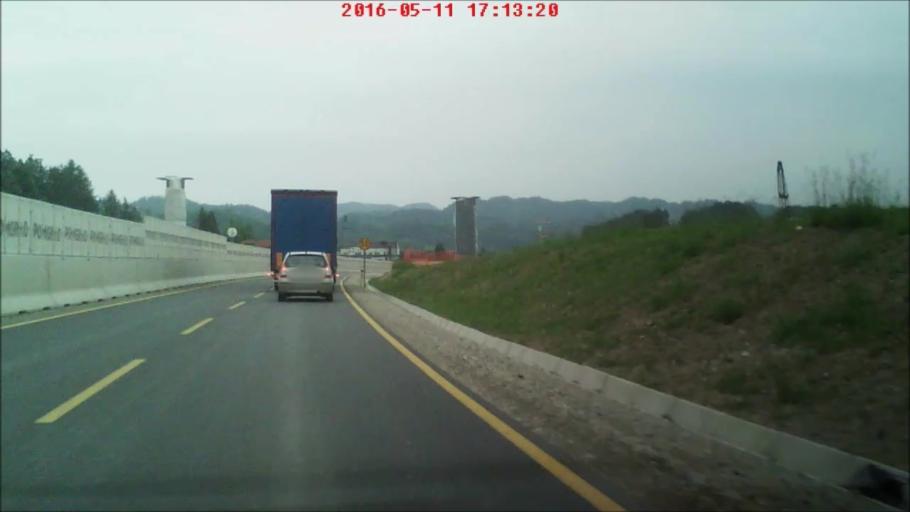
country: SI
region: Podlehnik
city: Podlehnik
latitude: 46.3412
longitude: 15.8747
